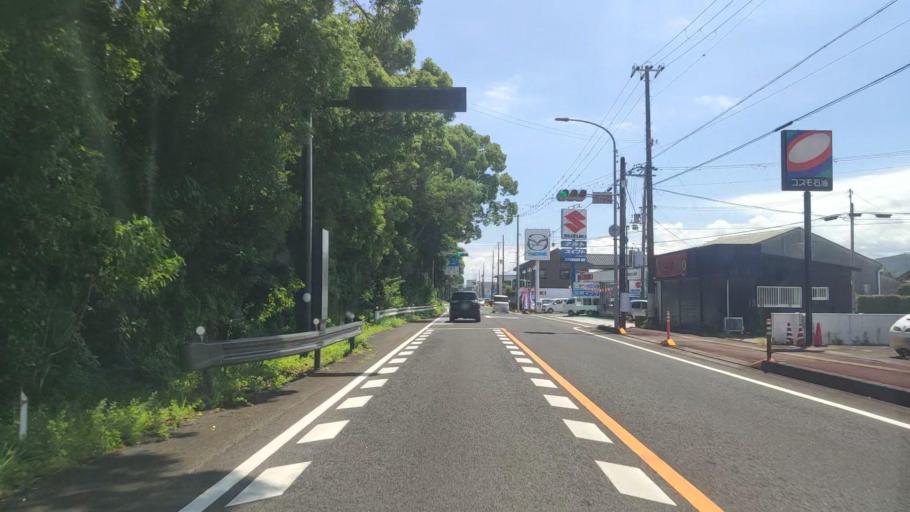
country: JP
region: Wakayama
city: Shingu
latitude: 33.8712
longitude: 136.0848
